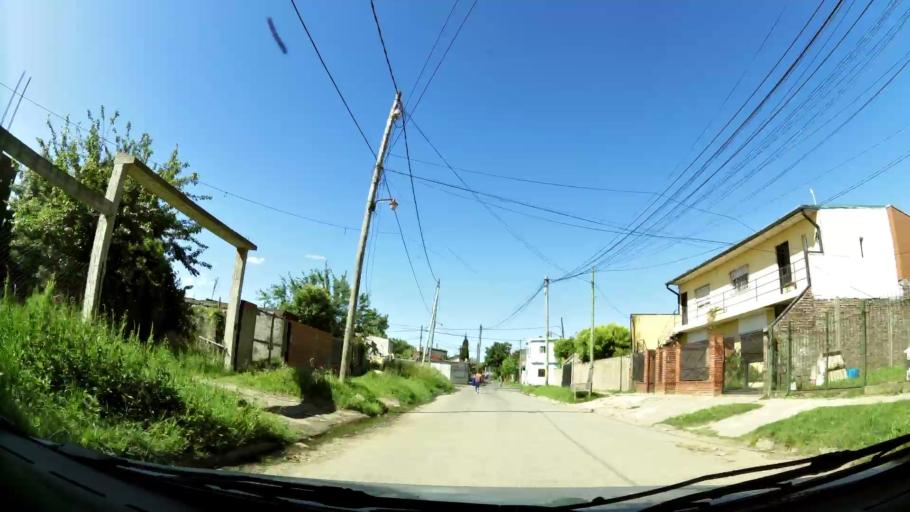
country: AR
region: Buenos Aires
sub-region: Partido de General San Martin
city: General San Martin
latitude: -34.5161
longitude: -58.5827
